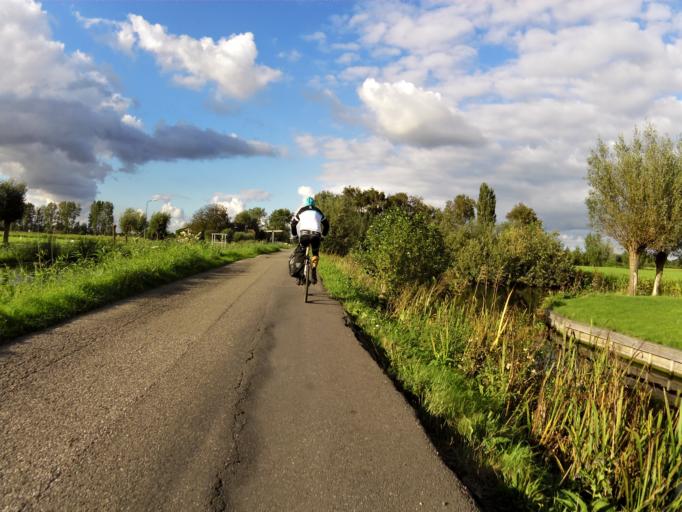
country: NL
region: Utrecht
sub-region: Gemeente Woerden
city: Woerden
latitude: 52.1370
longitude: 4.8935
